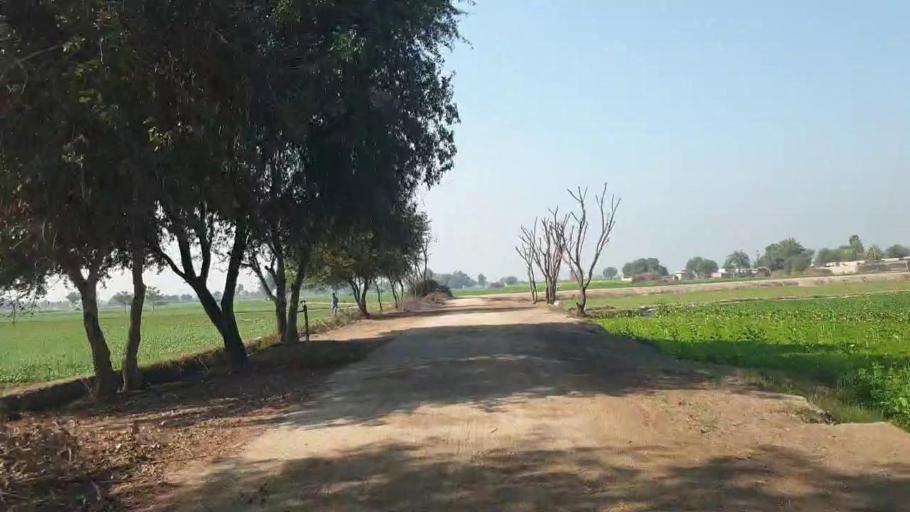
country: PK
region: Sindh
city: Shahdadpur
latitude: 25.9490
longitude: 68.5383
